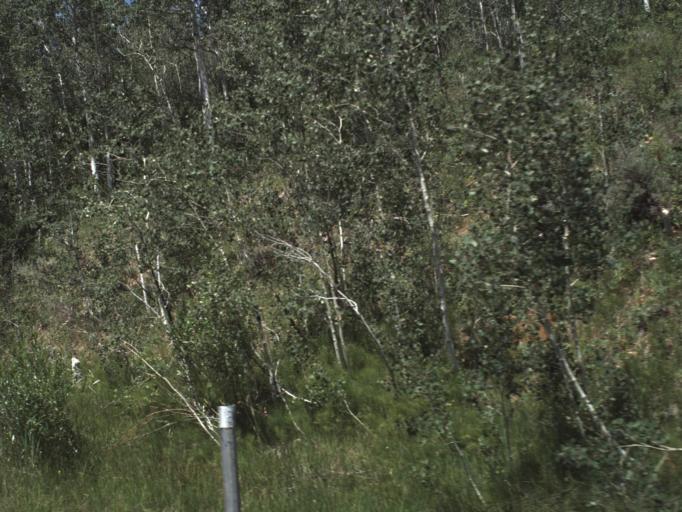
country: US
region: Utah
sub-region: Weber County
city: Wolf Creek
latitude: 41.3916
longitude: -111.5971
